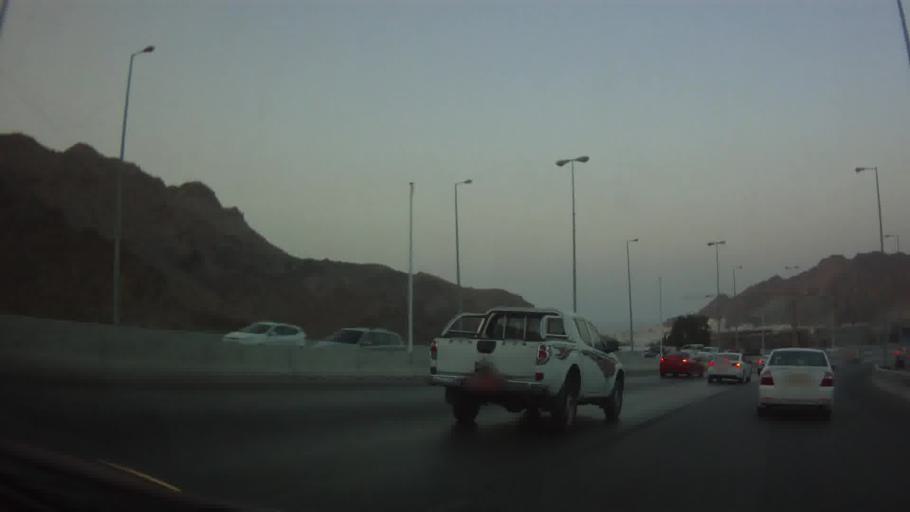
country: OM
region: Muhafazat Masqat
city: Muscat
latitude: 23.6195
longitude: 58.5349
